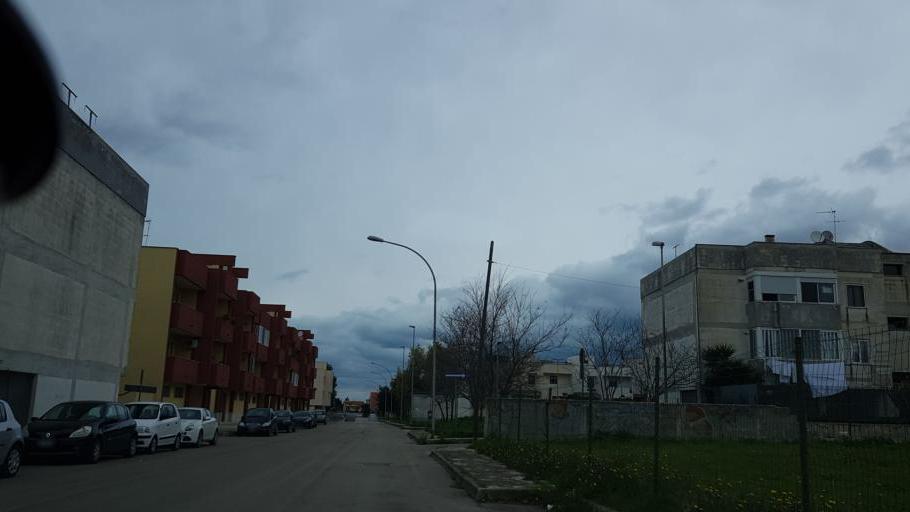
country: IT
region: Apulia
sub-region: Provincia di Brindisi
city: La Rosa
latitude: 40.6054
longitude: 17.9517
